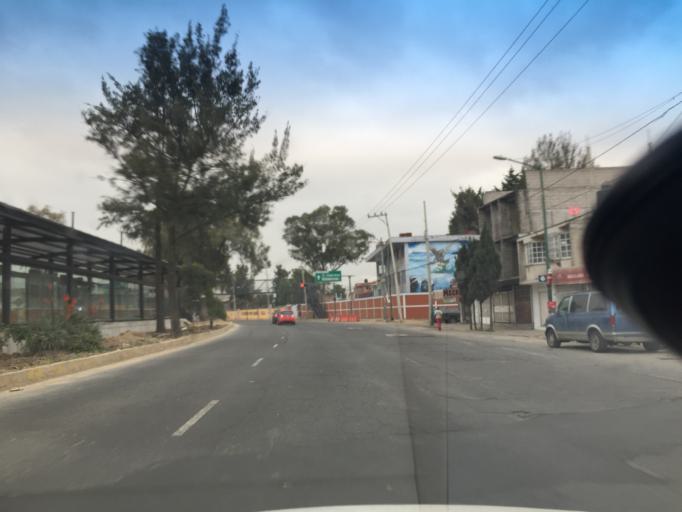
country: MX
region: Mexico City
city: Venustiano Carranza
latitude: 19.4670
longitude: -99.0752
